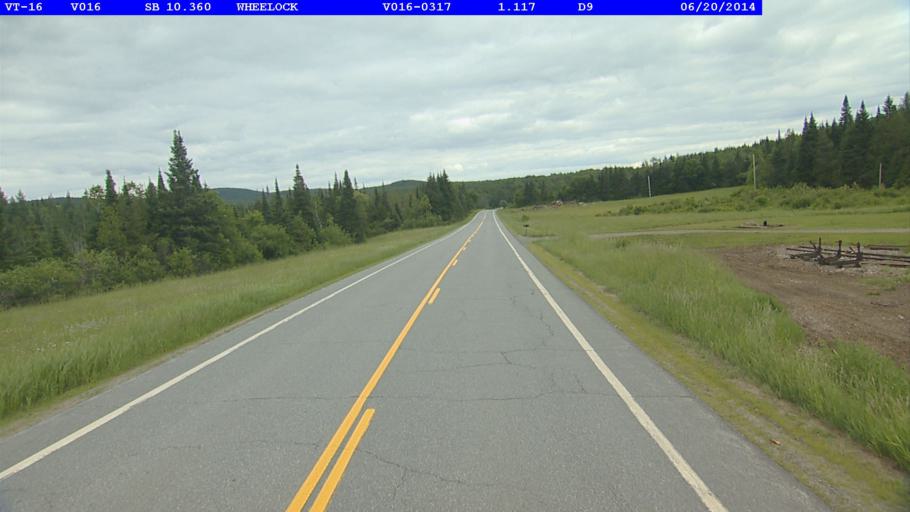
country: US
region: Vermont
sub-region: Caledonia County
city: Hardwick
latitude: 44.6127
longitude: -72.2080
